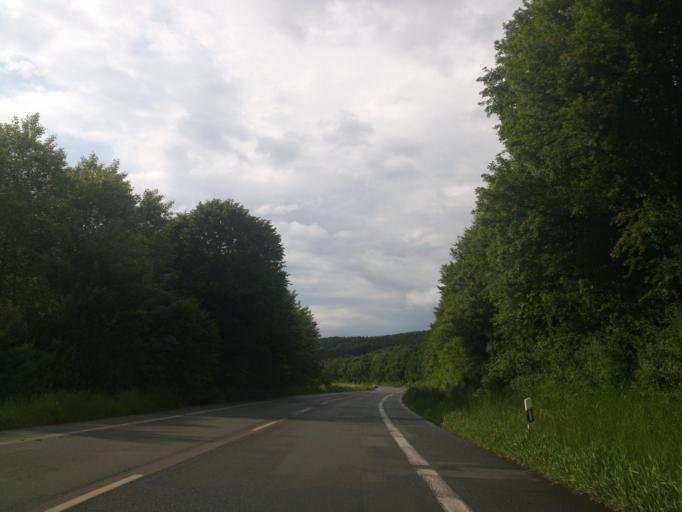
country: DE
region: North Rhine-Westphalia
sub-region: Regierungsbezirk Detmold
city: Willebadessen
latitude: 51.6397
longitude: 9.0202
